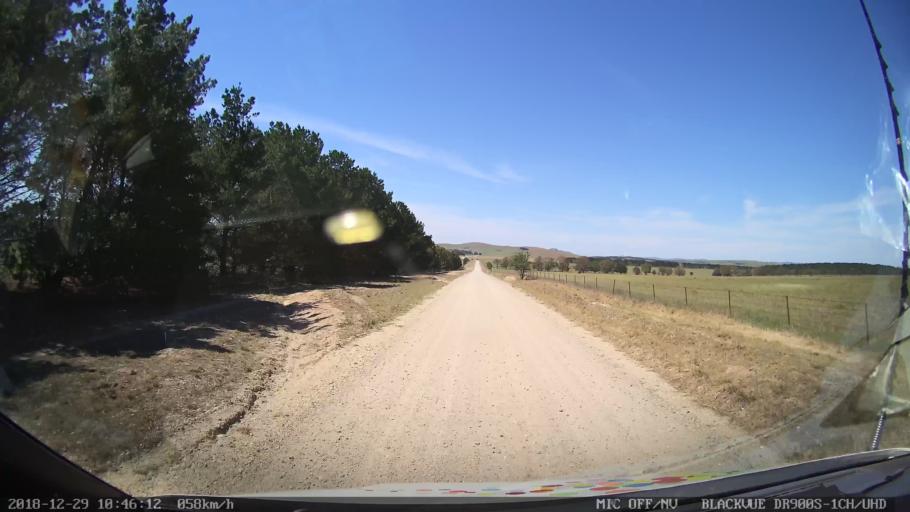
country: AU
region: New South Wales
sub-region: Palerang
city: Bungendore
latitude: -35.0483
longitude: 149.5167
